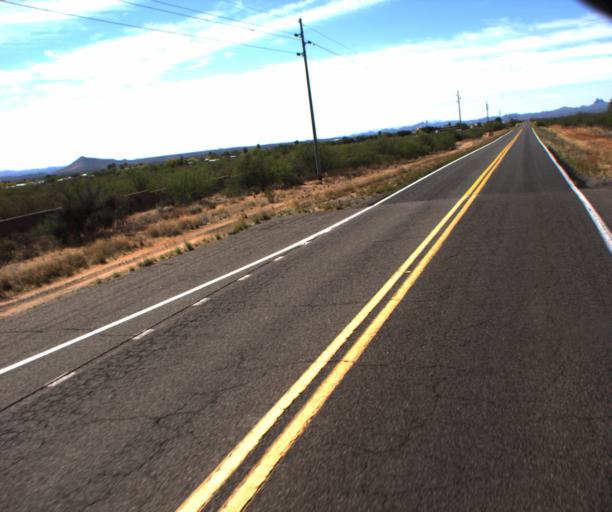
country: US
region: Arizona
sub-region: Yavapai County
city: Congress
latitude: 34.1099
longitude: -112.8330
